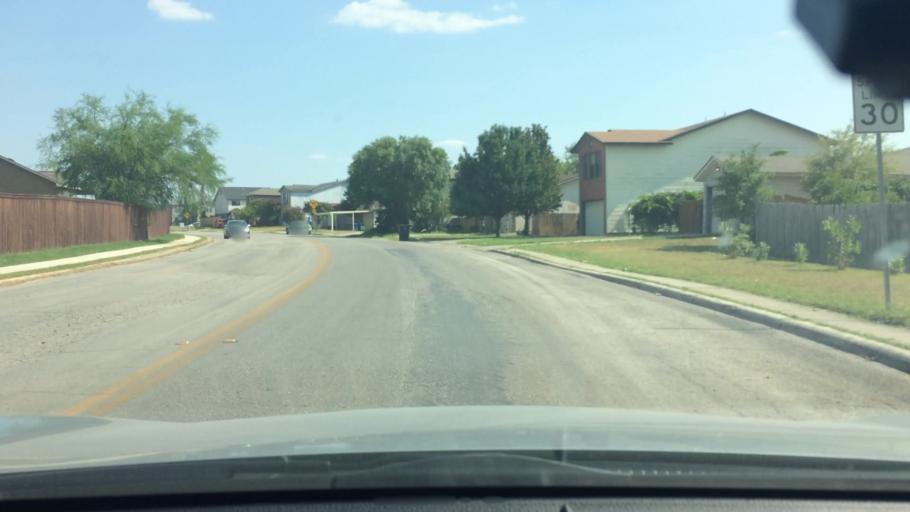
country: US
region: Texas
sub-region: Bexar County
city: Kirby
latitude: 29.4720
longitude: -98.3753
